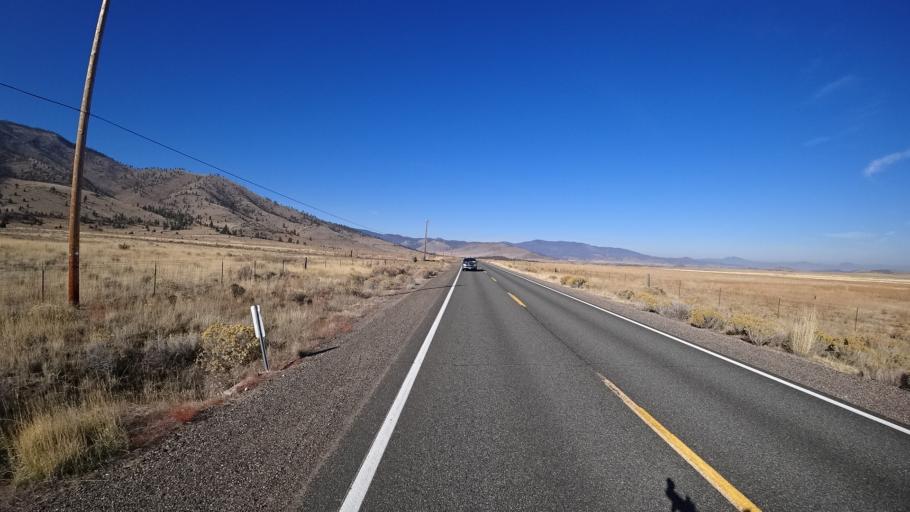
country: US
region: California
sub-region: Siskiyou County
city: Weed
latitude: 41.4771
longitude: -122.4893
